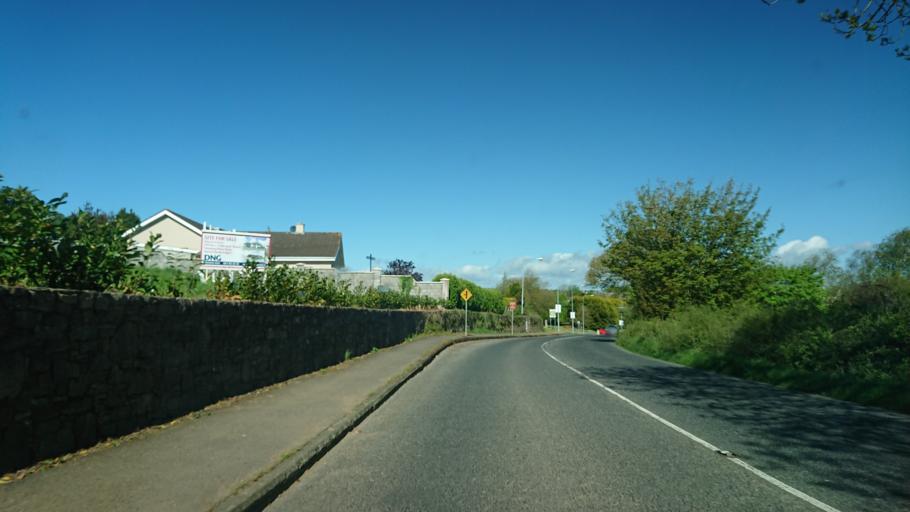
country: IE
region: Munster
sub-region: Waterford
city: Waterford
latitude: 52.2354
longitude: -7.0576
